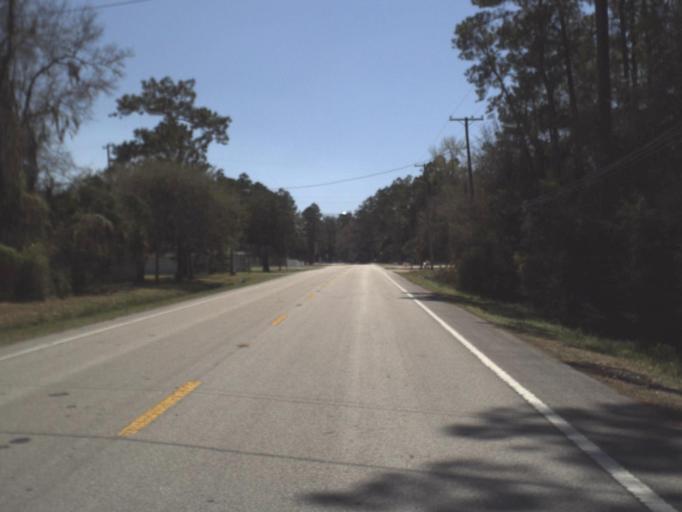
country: US
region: Florida
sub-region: Leon County
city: Woodville
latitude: 30.1660
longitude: -84.2077
